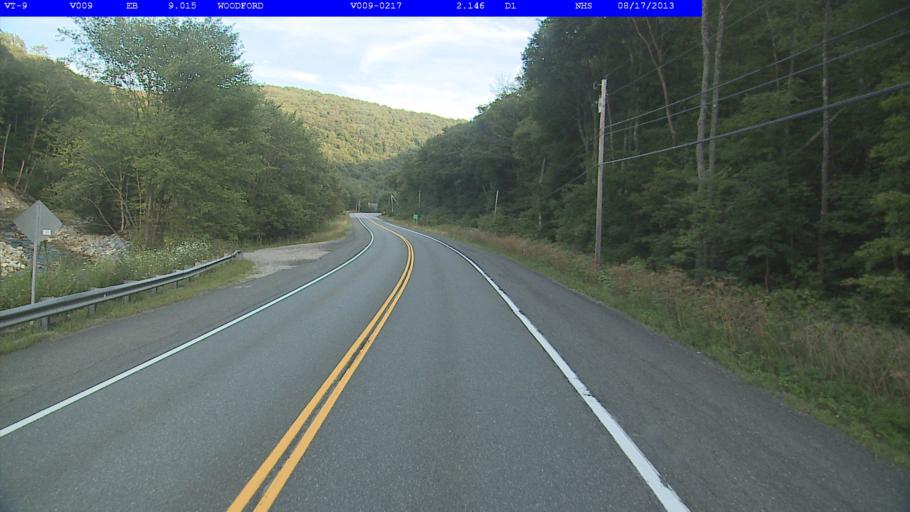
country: US
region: Vermont
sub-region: Bennington County
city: Bennington
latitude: 42.8887
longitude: -73.1204
